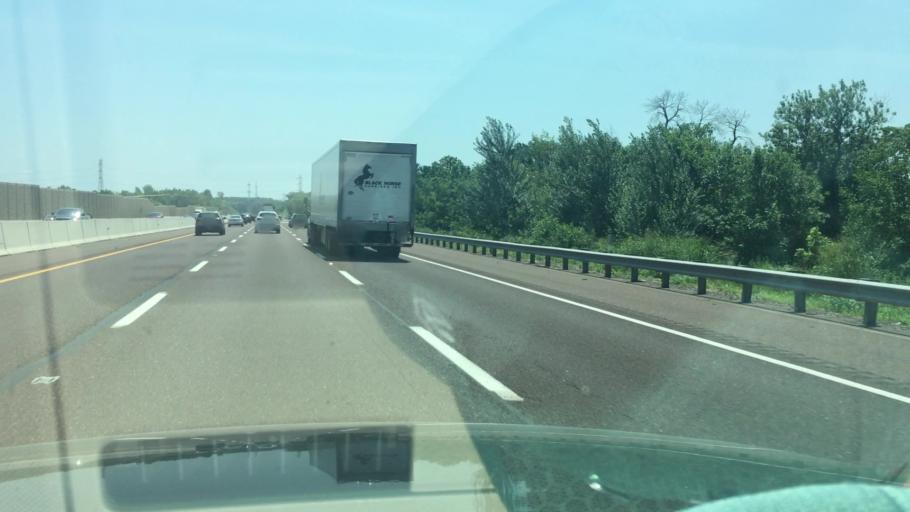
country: US
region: Pennsylvania
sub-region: Montgomery County
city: North Wales
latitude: 40.1804
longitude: -75.3102
